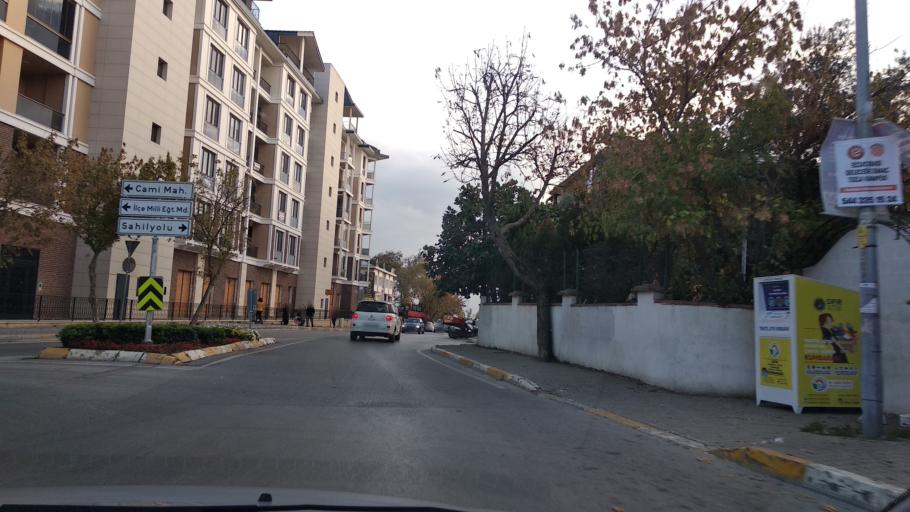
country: TR
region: Istanbul
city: Icmeler
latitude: 40.8185
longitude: 29.2984
